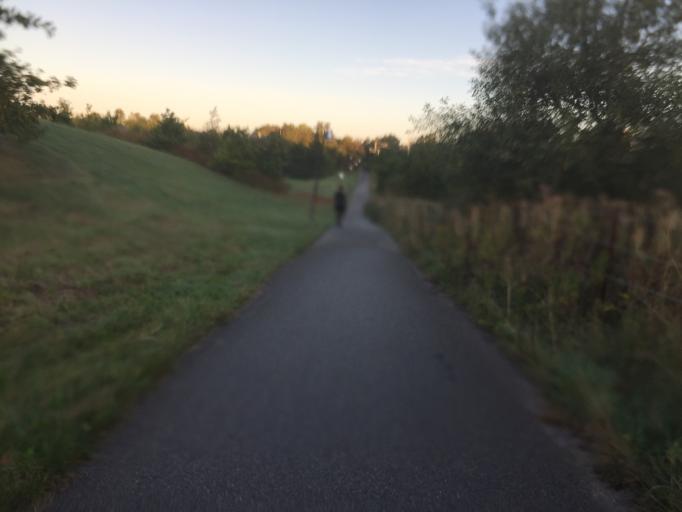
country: DK
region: Capital Region
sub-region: Ballerup Kommune
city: Malov
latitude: 55.7488
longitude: 12.3150
